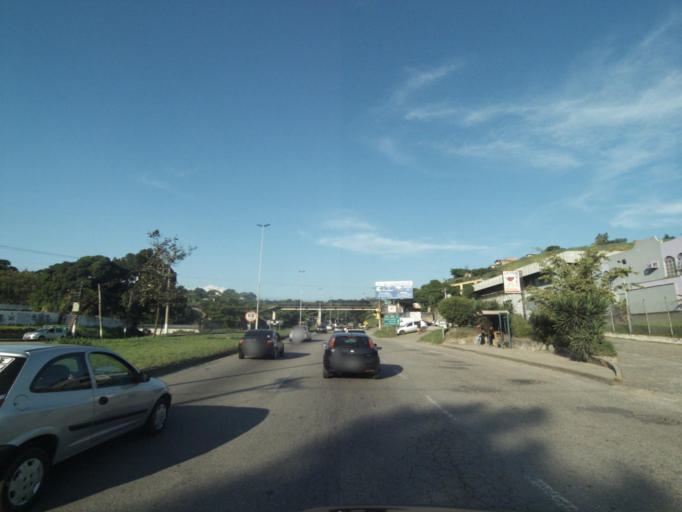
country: BR
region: Rio de Janeiro
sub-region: Niteroi
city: Niteroi
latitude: -22.8827
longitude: -43.0667
